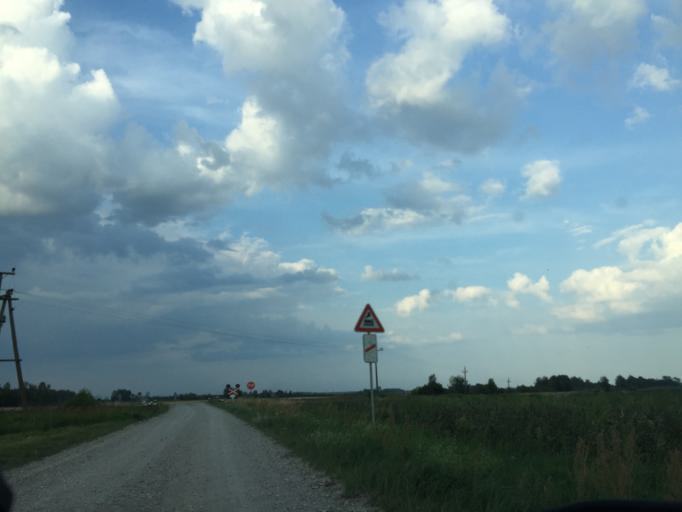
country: LV
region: Dobeles Rajons
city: Dobele
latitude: 56.6105
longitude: 23.3458
